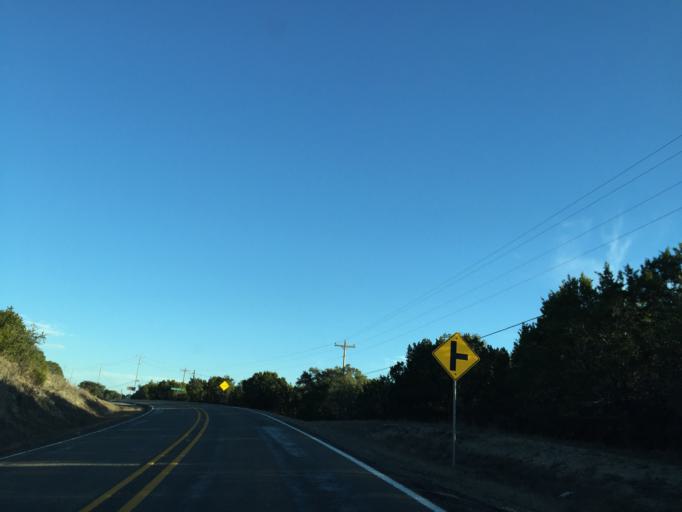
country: US
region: Texas
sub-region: Travis County
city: Lago Vista
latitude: 30.5114
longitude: -98.0401
